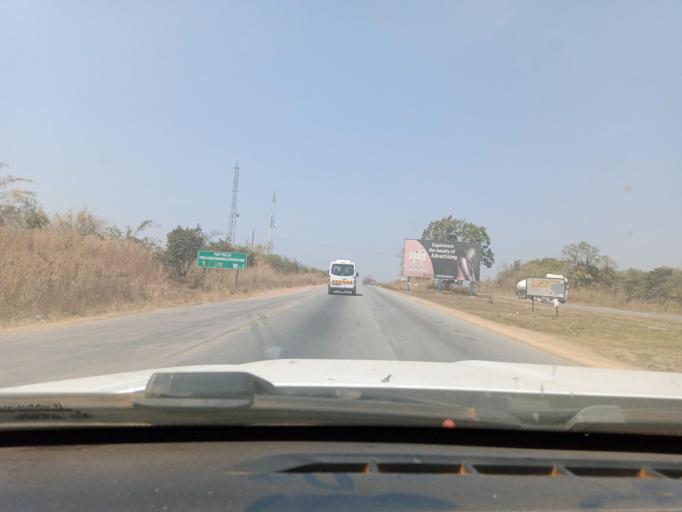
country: ZM
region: Copperbelt
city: Luanshya
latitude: -13.0218
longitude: 28.4416
